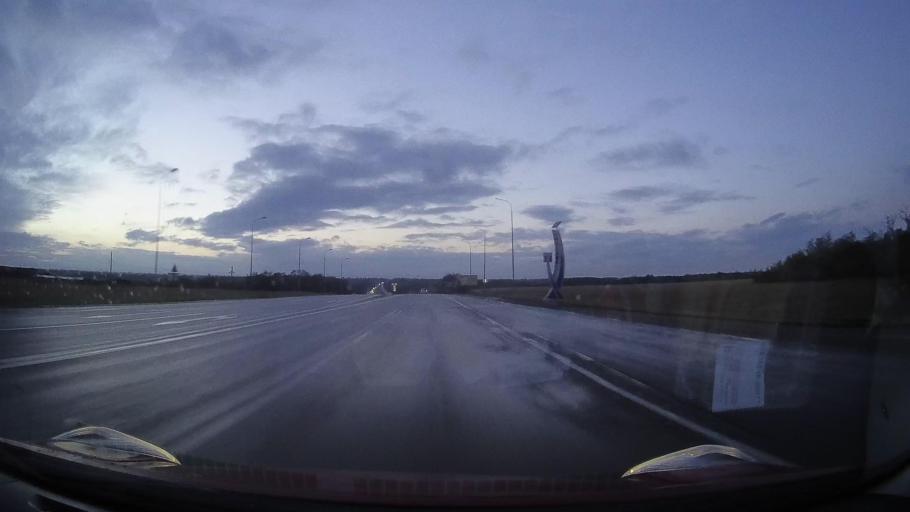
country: RU
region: Krasnodarskiy
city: Zavetnyy
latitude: 44.9105
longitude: 41.1640
